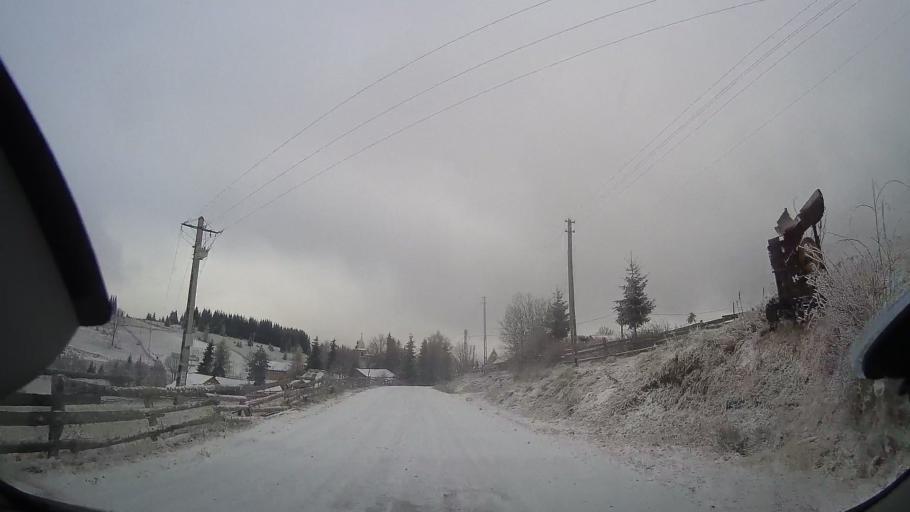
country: RO
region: Cluj
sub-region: Comuna Marisel
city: Marisel
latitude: 46.6596
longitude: 23.1302
